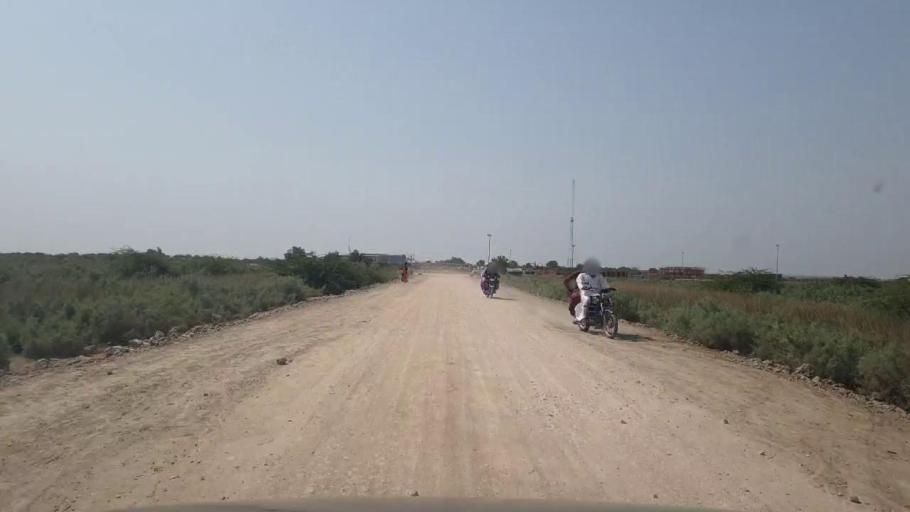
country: PK
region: Sindh
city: Jati
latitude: 24.3609
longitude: 68.5561
